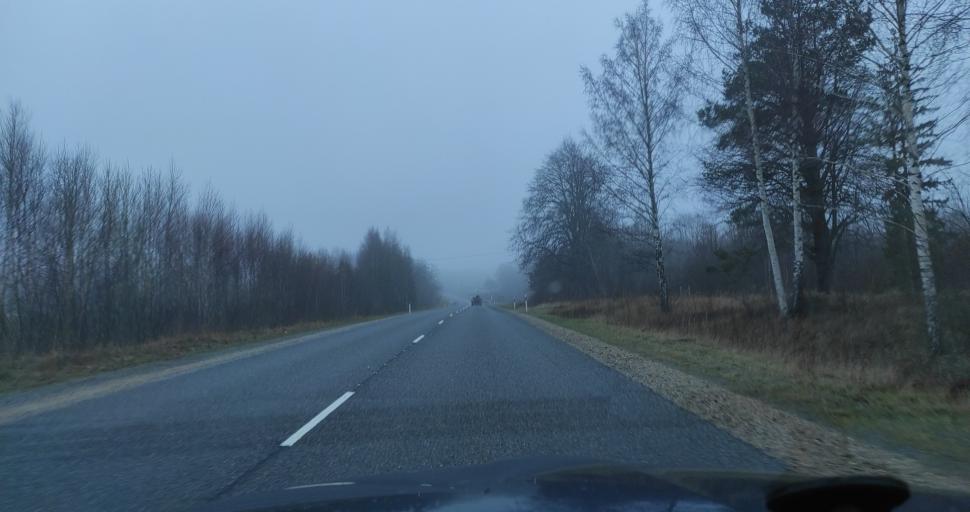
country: LV
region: Pavilostas
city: Pavilosta
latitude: 56.9743
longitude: 21.3530
